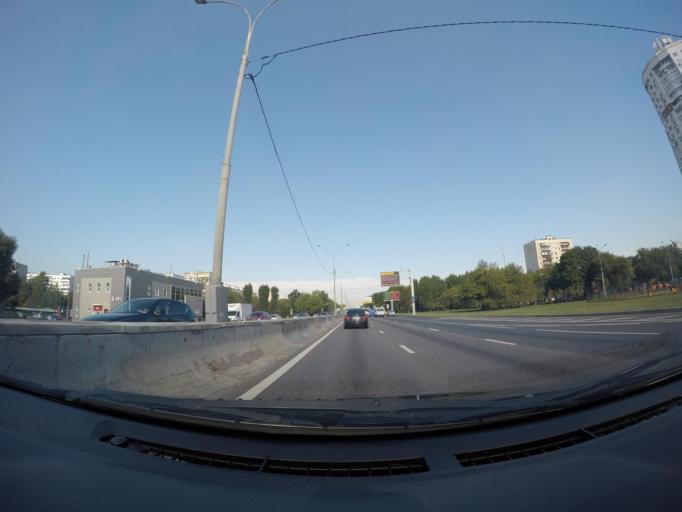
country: RU
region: Moscow
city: Vykhino-Zhulebino
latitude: 55.6948
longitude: 37.8112
